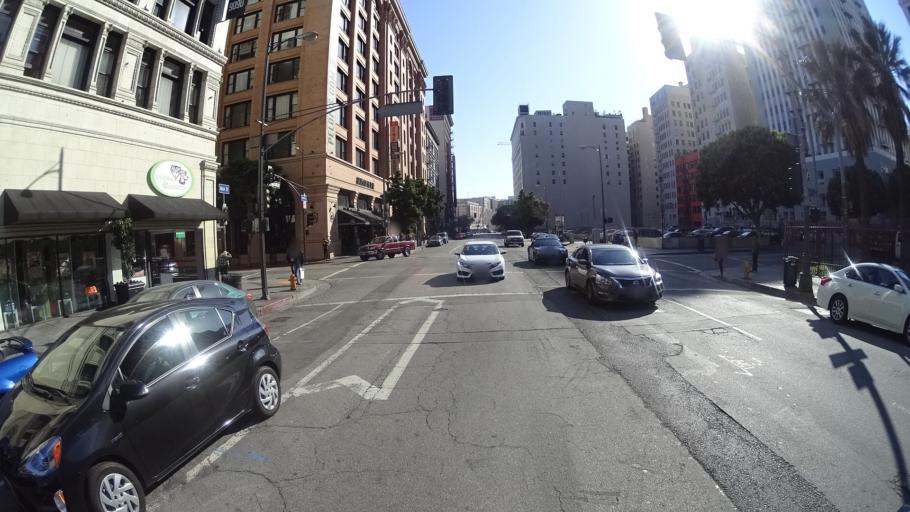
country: US
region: California
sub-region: Los Angeles County
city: Los Angeles
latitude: 34.0454
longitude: -118.2498
